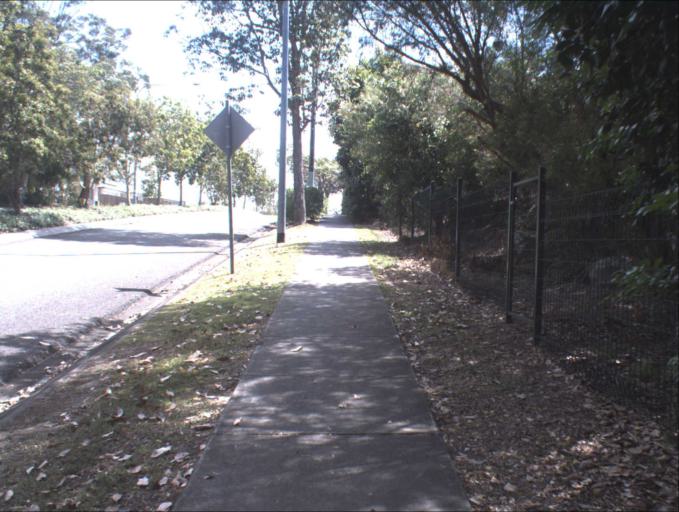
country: AU
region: Queensland
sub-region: Logan
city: Slacks Creek
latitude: -27.6462
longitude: 153.1878
